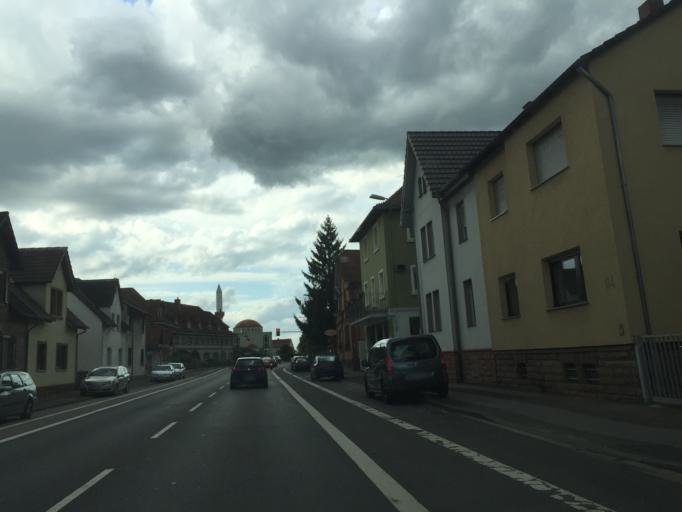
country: DE
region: Baden-Wuerttemberg
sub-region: Karlsruhe Region
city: Weinheim
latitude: 49.5612
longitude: 8.6672
